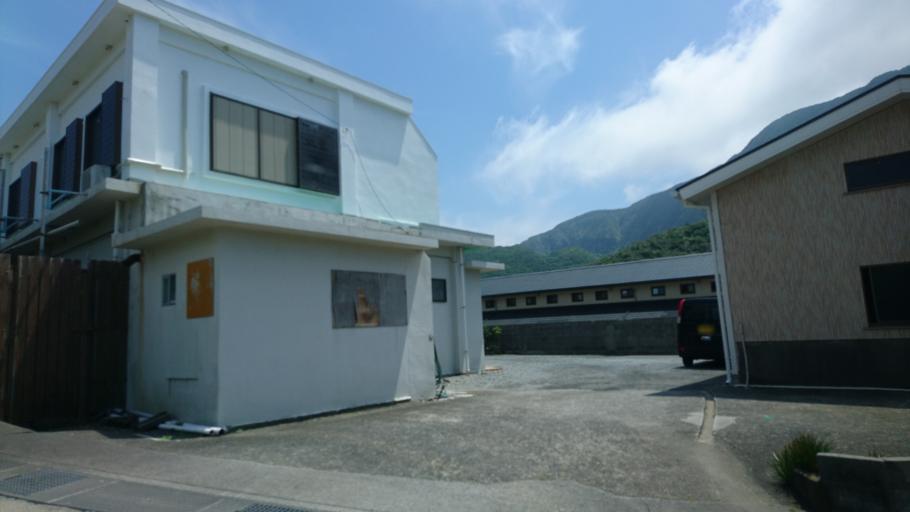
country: JP
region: Shizuoka
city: Shimoda
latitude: 34.4149
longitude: 139.2785
